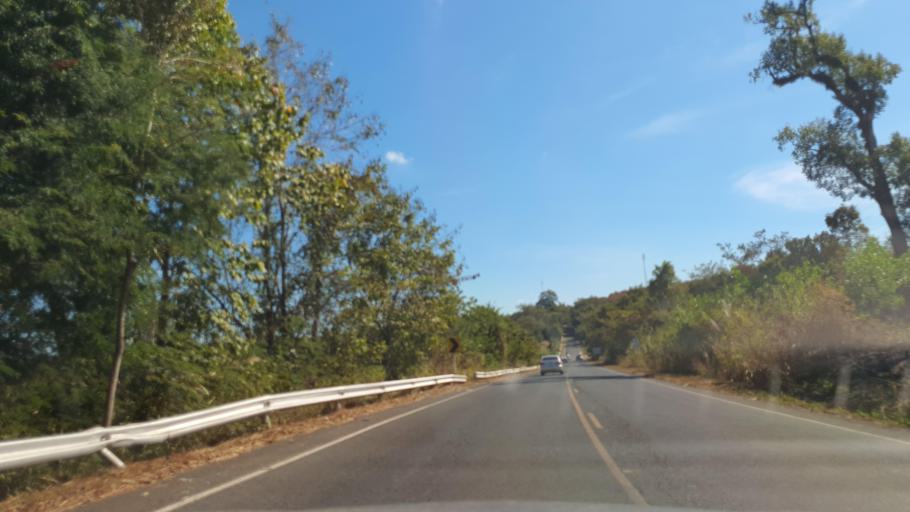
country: TH
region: Kalasin
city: Khao Wong
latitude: 16.7750
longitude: 104.1531
